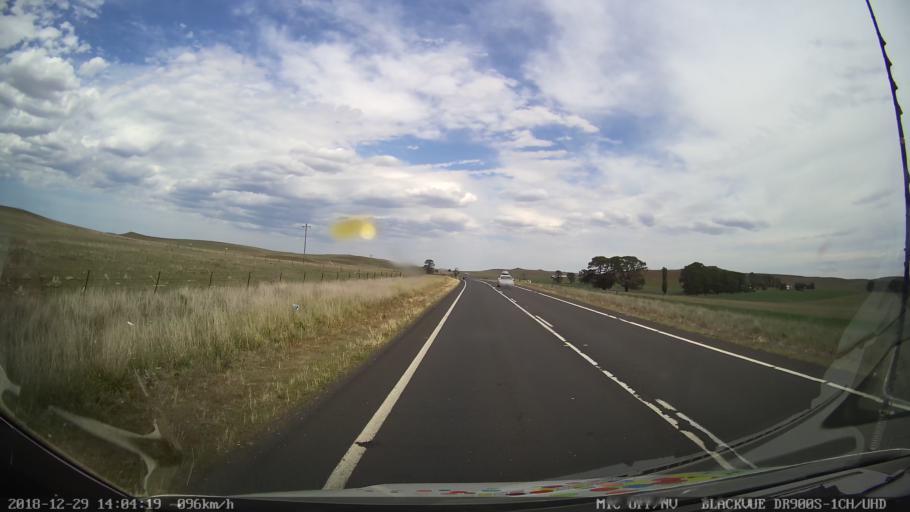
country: AU
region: New South Wales
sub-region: Cooma-Monaro
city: Cooma
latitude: -36.3143
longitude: 149.1862
